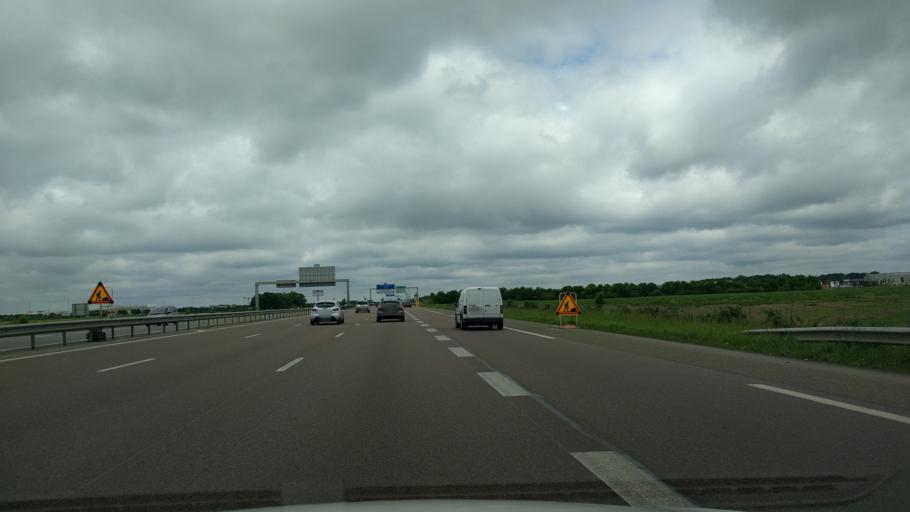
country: FR
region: Ile-de-France
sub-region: Departement de Seine-et-Marne
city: Nandy
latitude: 48.6127
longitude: 2.5688
